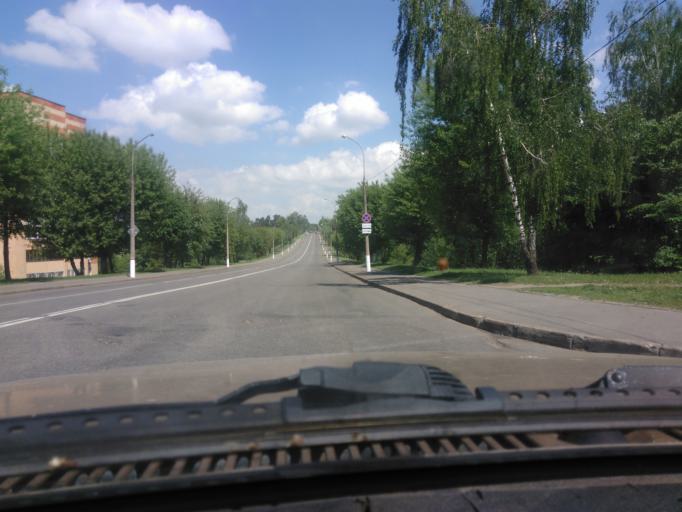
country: BY
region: Mogilev
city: Mahilyow
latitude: 53.9210
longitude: 30.3116
